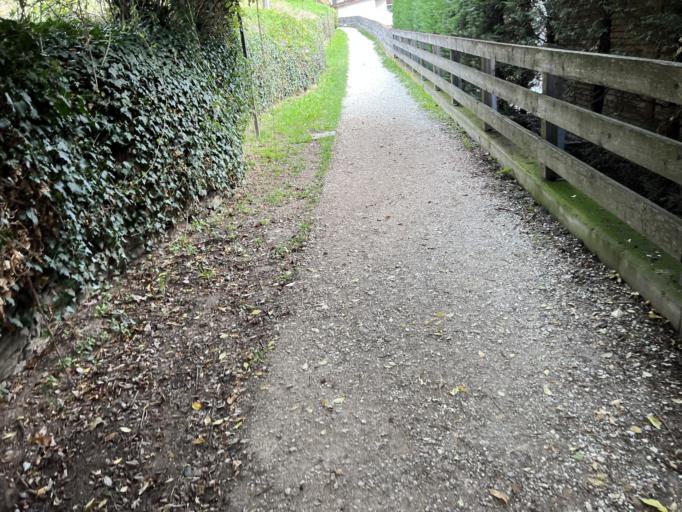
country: IT
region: Trentino-Alto Adige
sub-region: Bolzano
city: Naturno
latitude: 46.6535
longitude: 11.0062
